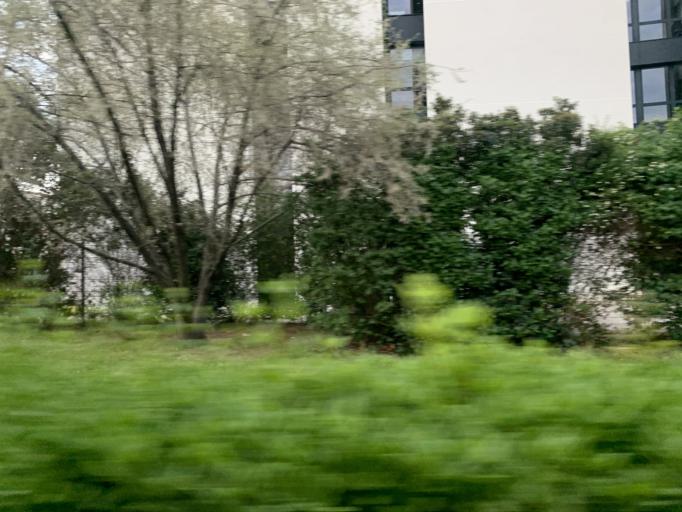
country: FR
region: Rhone-Alpes
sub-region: Departement du Rhone
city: Villeurbanne
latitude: 45.7566
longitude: 4.8980
